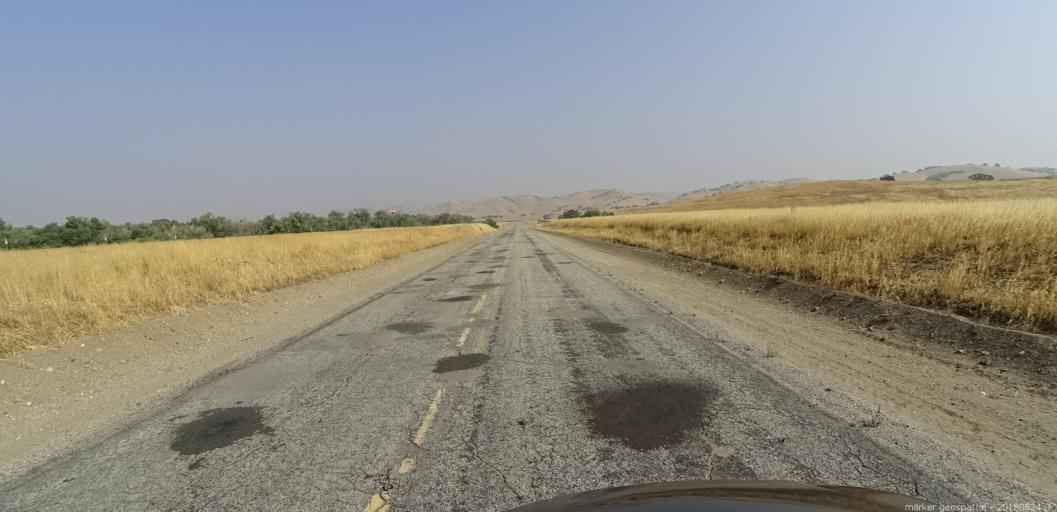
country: US
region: California
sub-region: San Luis Obispo County
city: San Miguel
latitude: 35.8384
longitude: -120.7515
